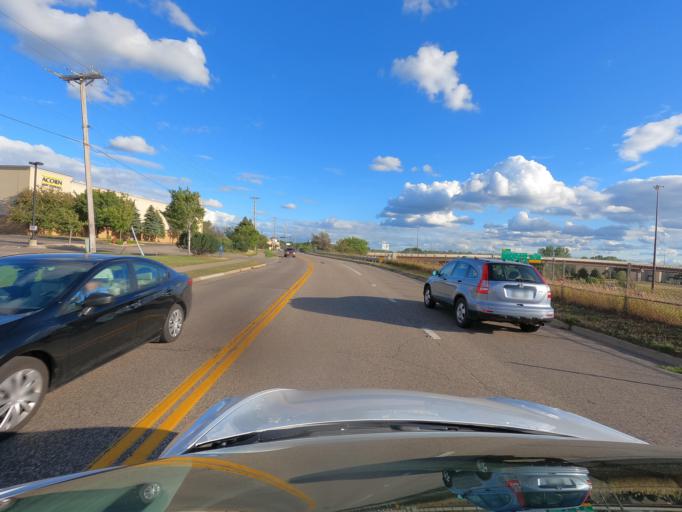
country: US
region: Minnesota
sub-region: Ramsey County
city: Lauderdale
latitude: 45.0163
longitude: -93.1871
